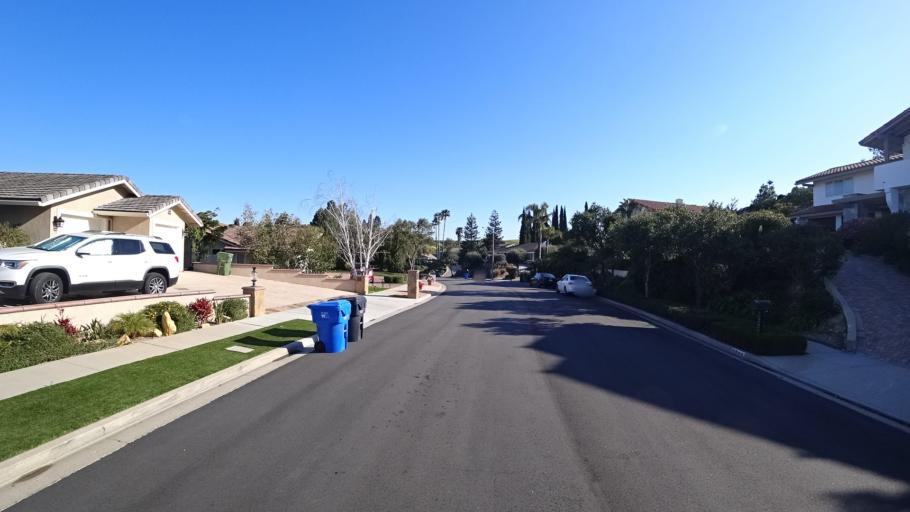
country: US
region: California
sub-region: Ventura County
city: Thousand Oaks
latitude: 34.1946
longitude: -118.8339
